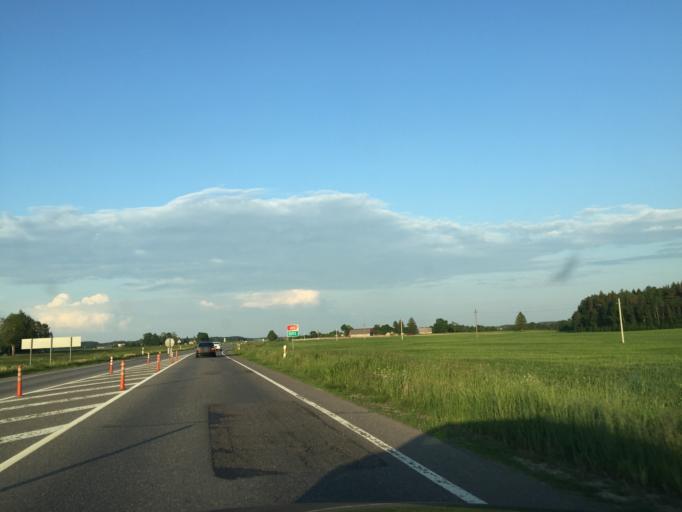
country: LT
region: Telsiu apskritis
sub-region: Telsiai
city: Telsiai
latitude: 56.0025
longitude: 22.4346
